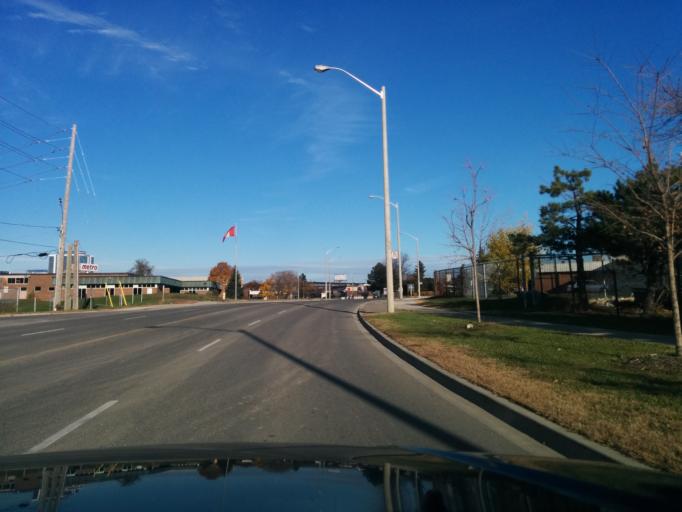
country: CA
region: Ontario
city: Etobicoke
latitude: 43.6185
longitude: -79.5653
